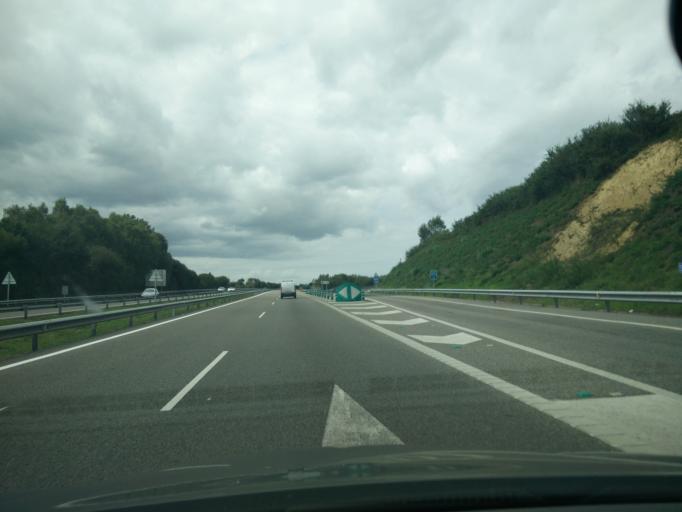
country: ES
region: Galicia
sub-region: Provincia da Coruna
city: Oleiros
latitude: 43.2962
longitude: -8.3062
